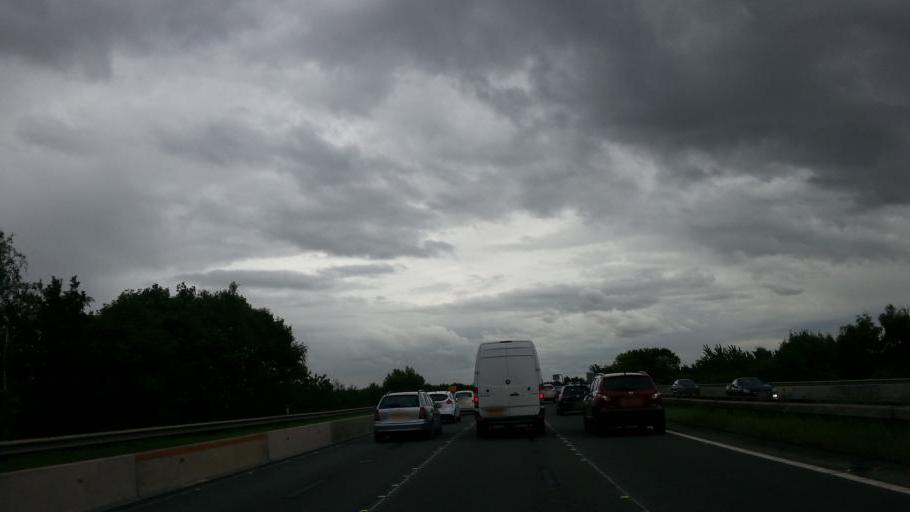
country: GB
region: England
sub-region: City and Borough of Wakefield
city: Normanton
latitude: 53.7242
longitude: -1.4313
